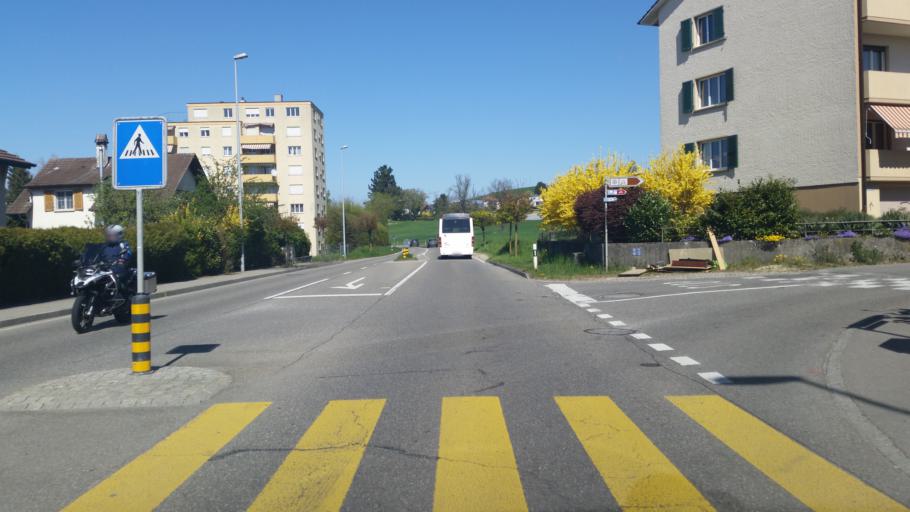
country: CH
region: Fribourg
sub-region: See District
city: Murten
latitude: 46.9409
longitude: 7.1466
